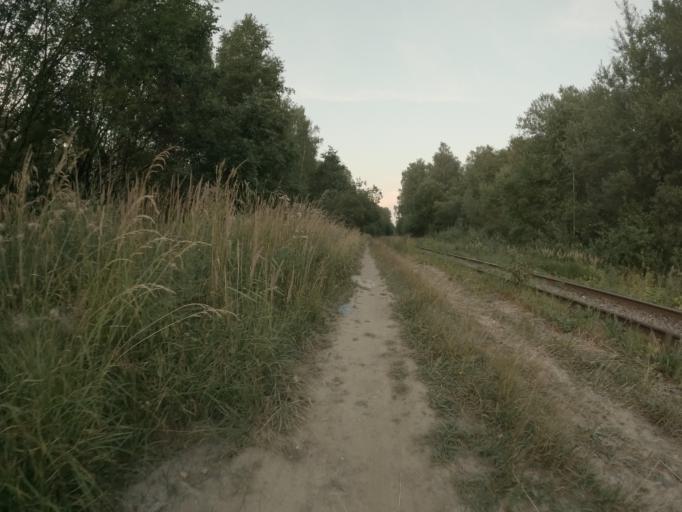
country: RU
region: St.-Petersburg
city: Krasnogvargeisky
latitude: 59.9436
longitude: 30.5228
